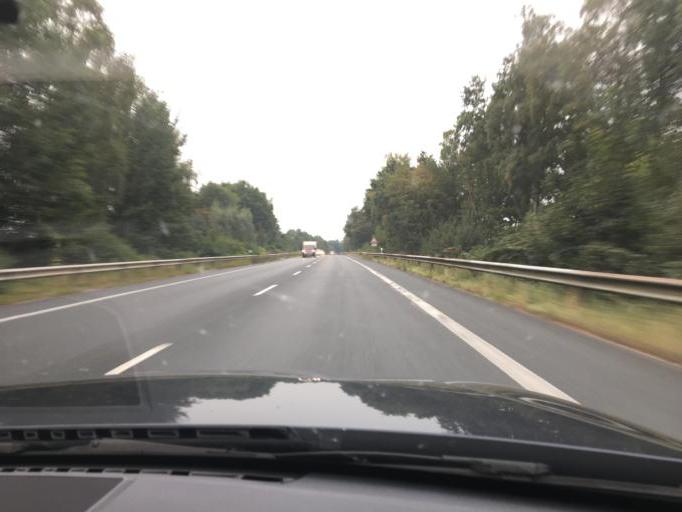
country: DE
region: North Rhine-Westphalia
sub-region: Regierungsbezirk Munster
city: Greven
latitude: 52.0478
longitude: 7.6821
